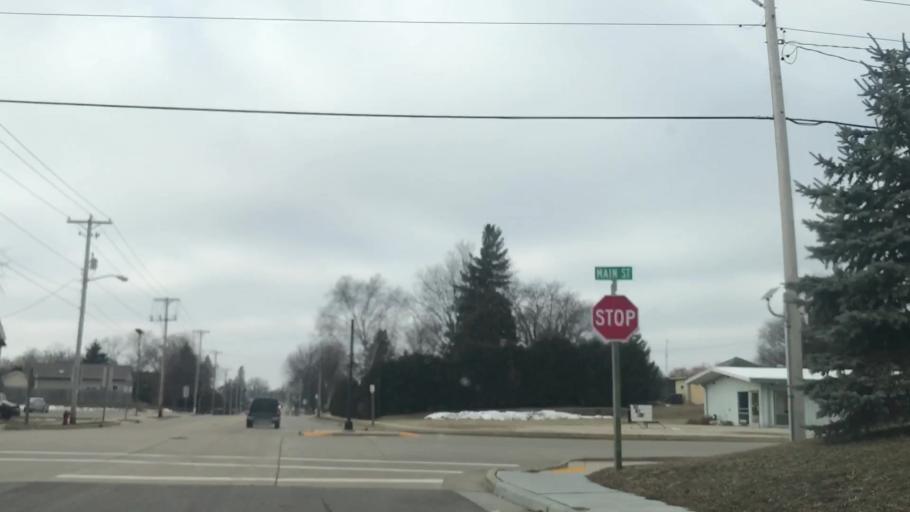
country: US
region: Wisconsin
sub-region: Dodge County
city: Horicon
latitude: 43.4442
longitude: -88.6394
